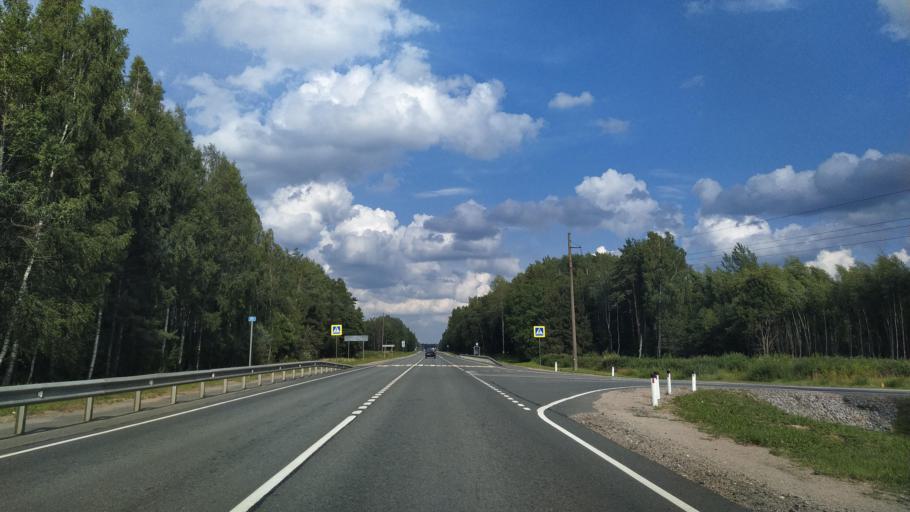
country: RU
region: Novgorod
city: Sol'tsy
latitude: 58.1709
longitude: 30.4948
